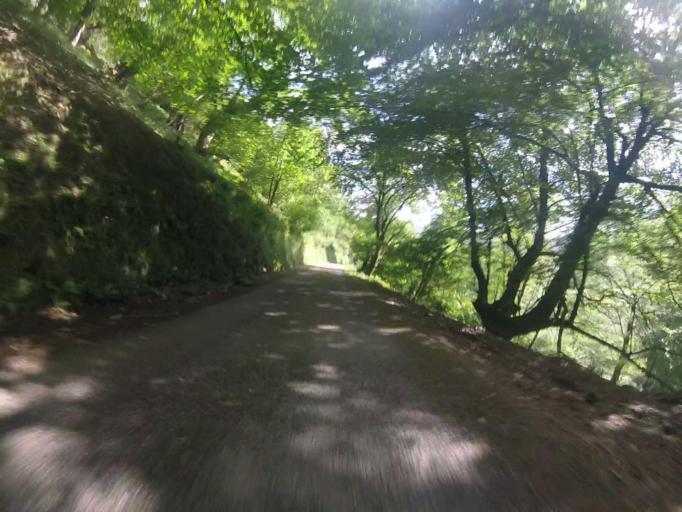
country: ES
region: Navarre
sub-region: Provincia de Navarra
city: Goizueta
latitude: 43.2191
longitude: -1.8056
